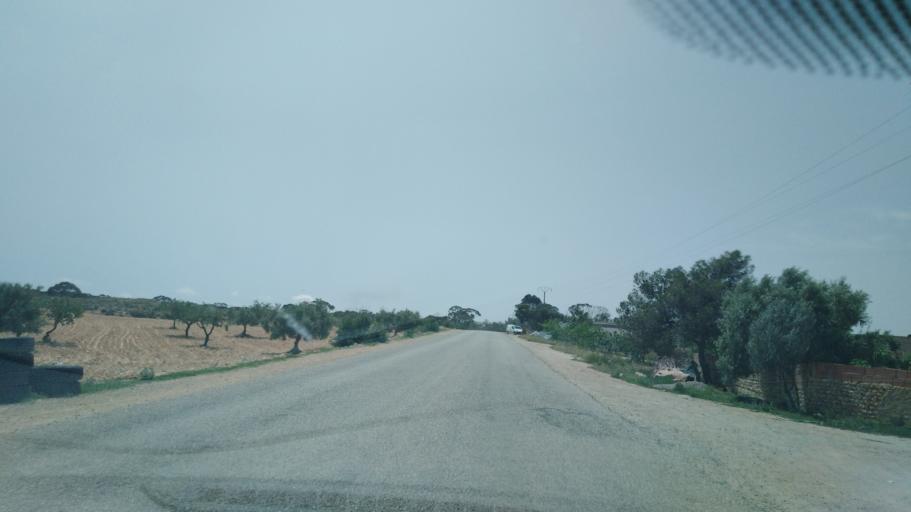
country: TN
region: Safaqis
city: Sfax
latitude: 34.7267
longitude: 10.5762
